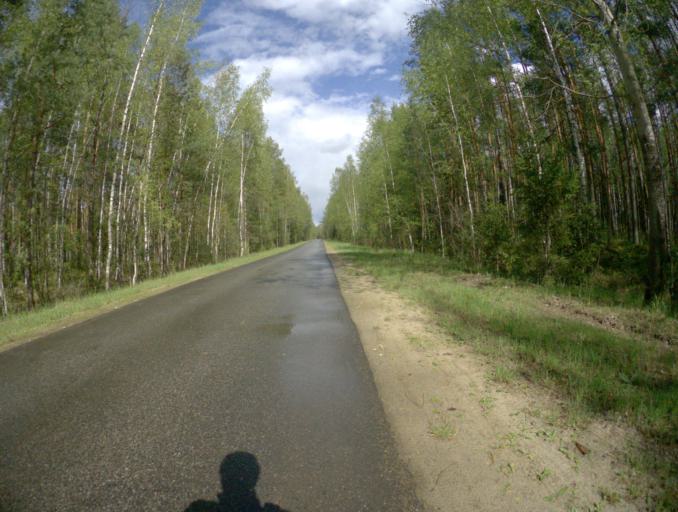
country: RU
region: Vladimir
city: Urshel'skiy
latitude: 55.5833
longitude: 40.2008
